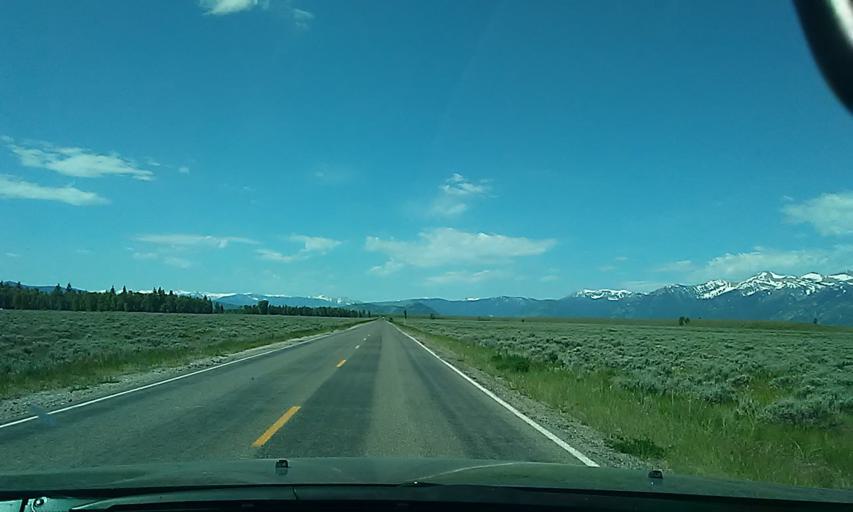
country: US
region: Wyoming
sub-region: Teton County
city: Jackson
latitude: 43.6169
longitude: -110.6754
